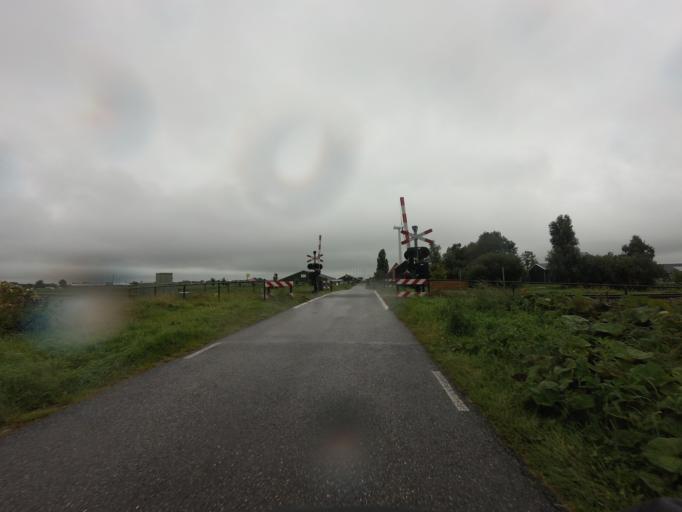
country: NL
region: Friesland
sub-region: Sudwest Fryslan
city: Workum
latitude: 52.9834
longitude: 5.4717
